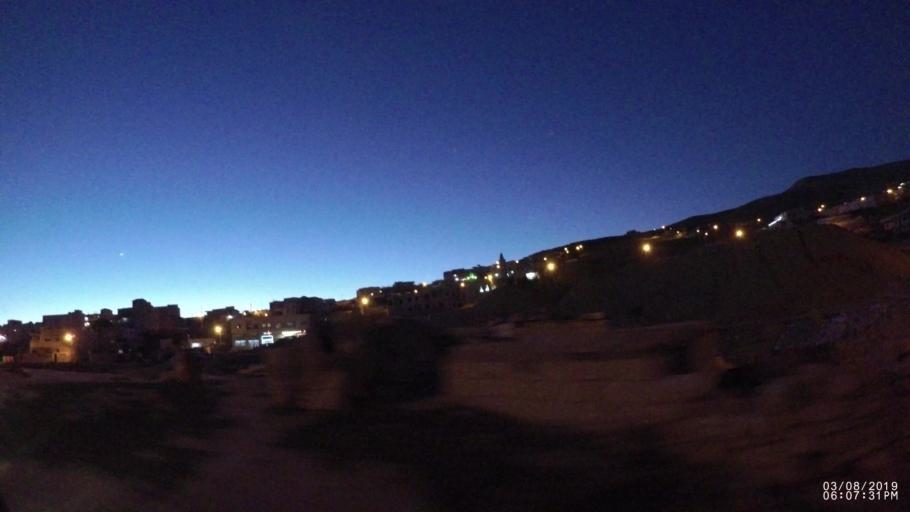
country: JO
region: Ma'an
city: Petra
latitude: 30.3293
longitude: 35.4768
